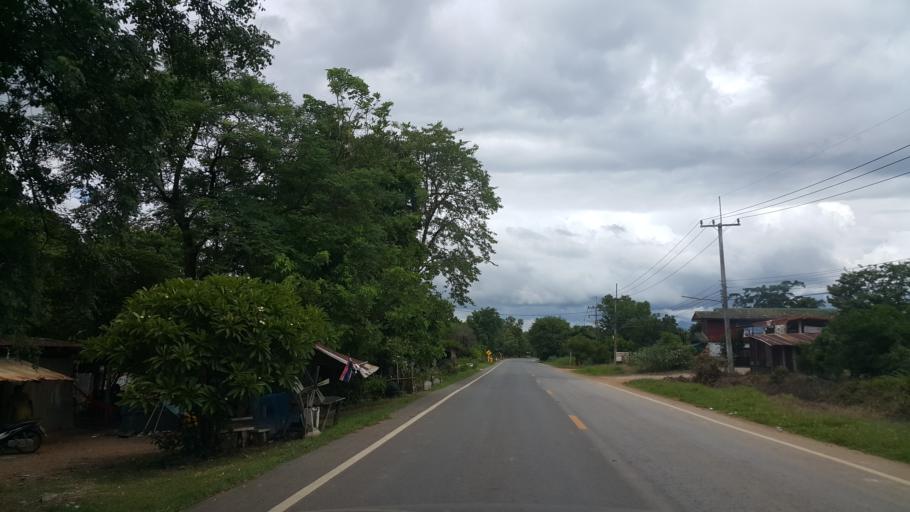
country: TH
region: Sukhothai
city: Ban Na
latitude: 17.0402
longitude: 99.7039
